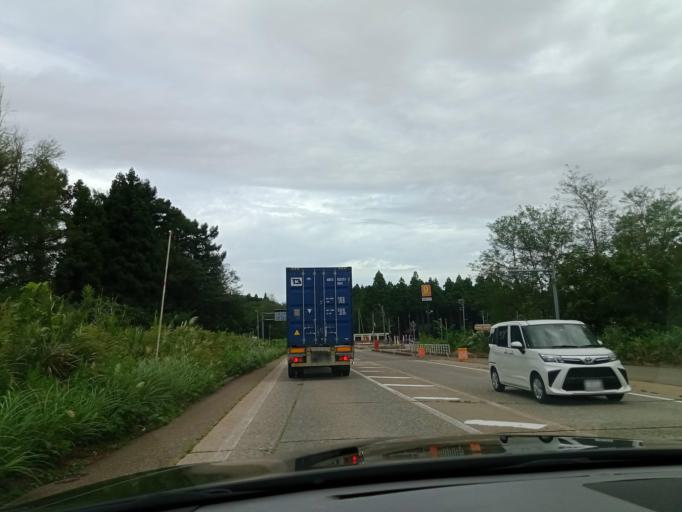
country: JP
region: Niigata
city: Arai
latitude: 36.9813
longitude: 138.2212
